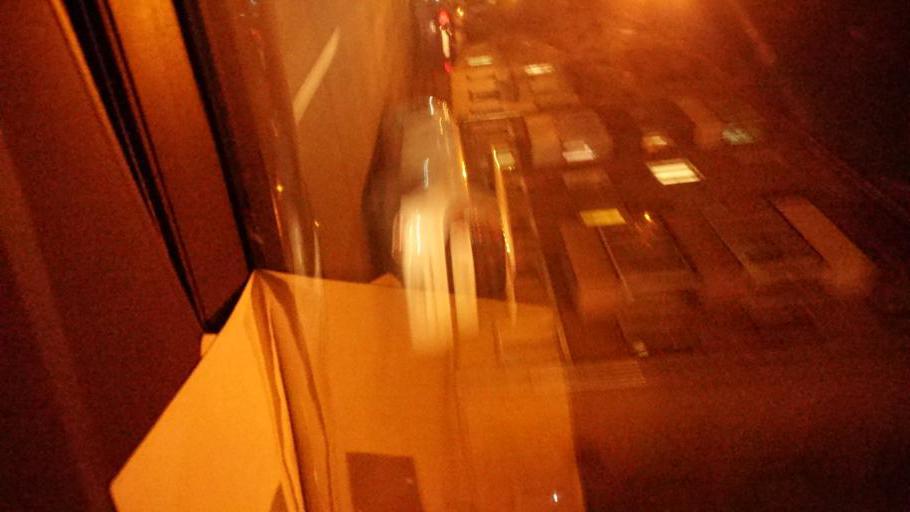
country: BY
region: Minsk
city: Minsk
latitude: 53.9298
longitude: 27.6005
